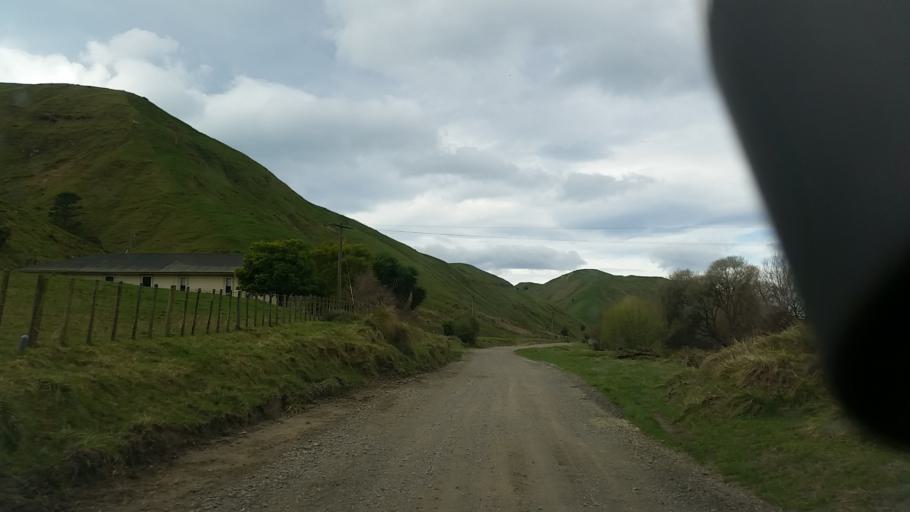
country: NZ
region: Hawke's Bay
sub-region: Napier City
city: Napier
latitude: -39.2694
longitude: 176.9823
